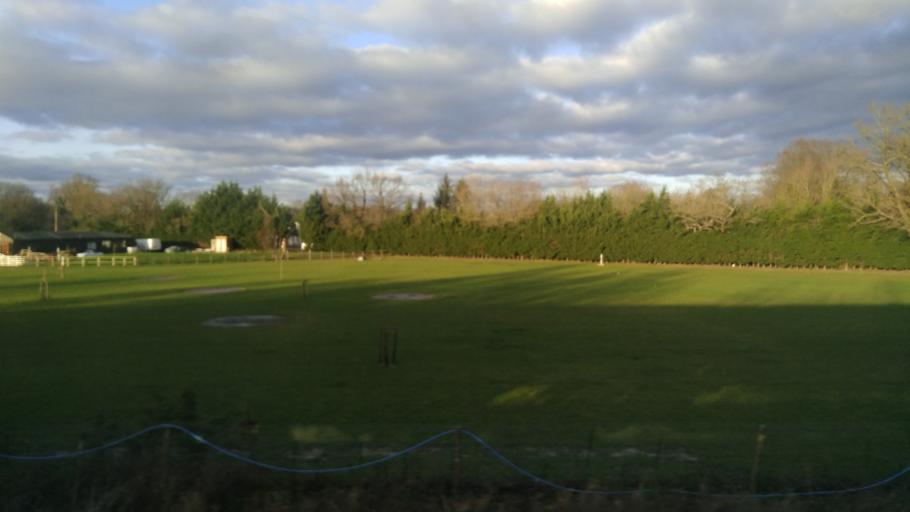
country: GB
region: England
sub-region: Kent
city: Headcorn
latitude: 51.1630
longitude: 0.6625
